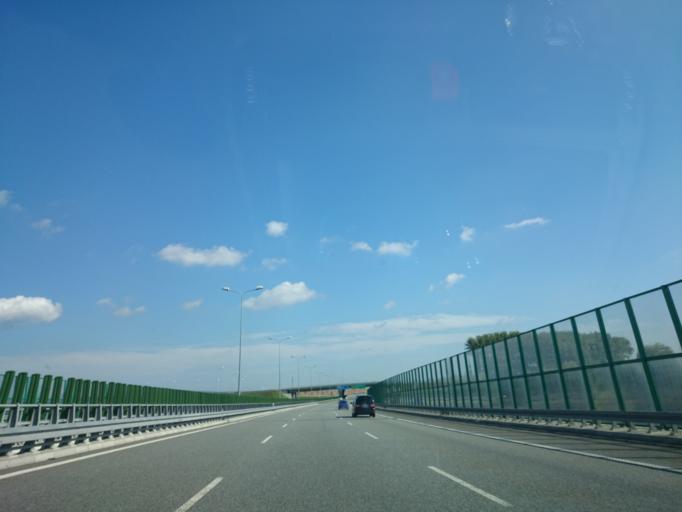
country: PL
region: Silesian Voivodeship
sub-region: Powiat gliwicki
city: Knurow
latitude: 50.2219
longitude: 18.6922
